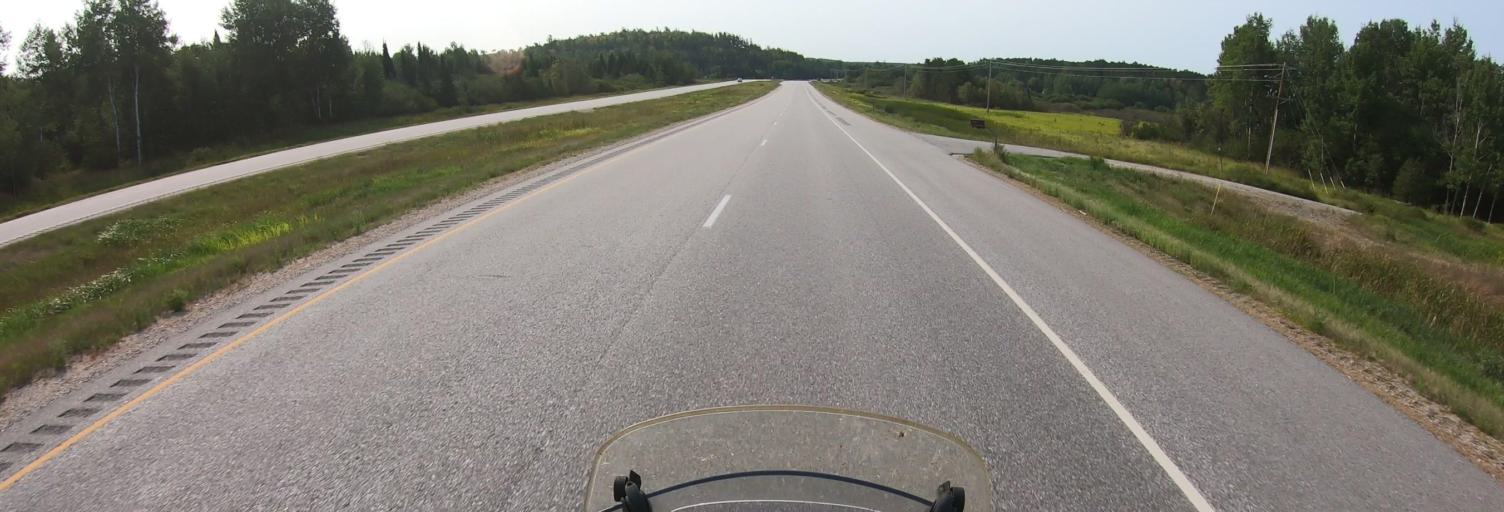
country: US
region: Minnesota
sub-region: Saint Louis County
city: Mountain Iron
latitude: 47.7138
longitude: -92.6484
